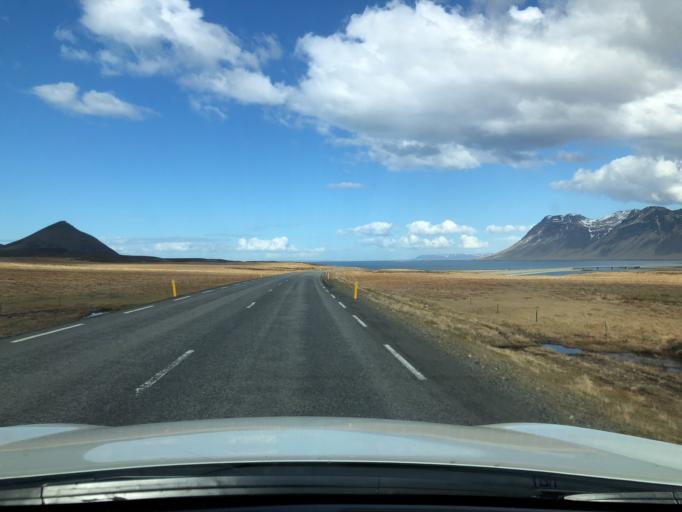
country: IS
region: West
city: Stykkisholmur
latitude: 64.9601
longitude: -23.1503
